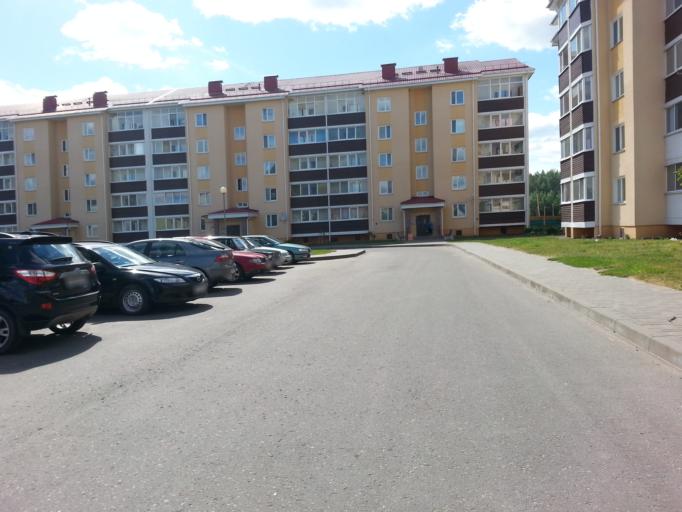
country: BY
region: Minsk
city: Narach
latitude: 54.9142
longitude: 26.7005
